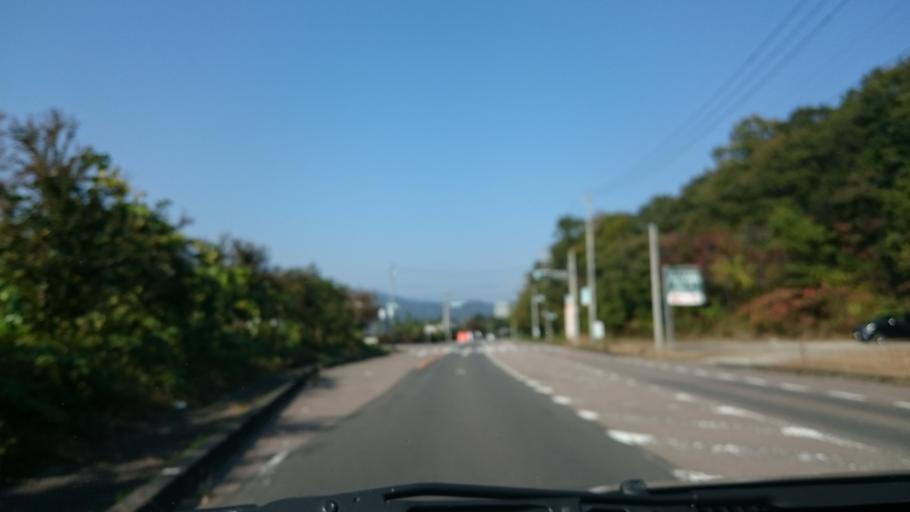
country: JP
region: Gifu
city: Nakatsugawa
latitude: 35.5388
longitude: 137.4480
